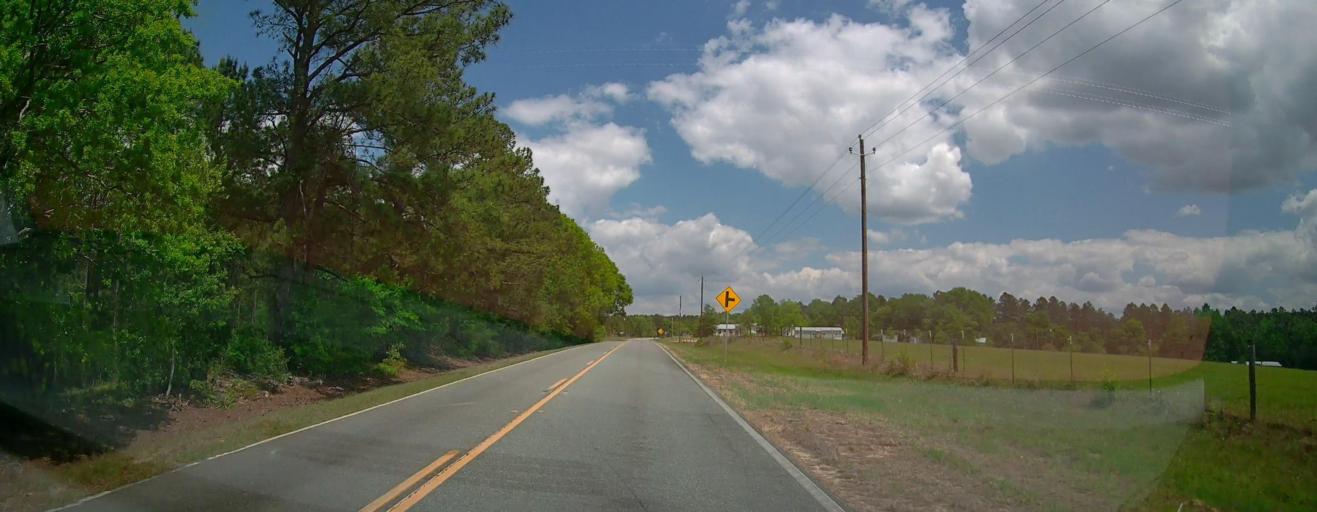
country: US
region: Georgia
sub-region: Laurens County
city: East Dublin
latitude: 32.5269
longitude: -82.7130
